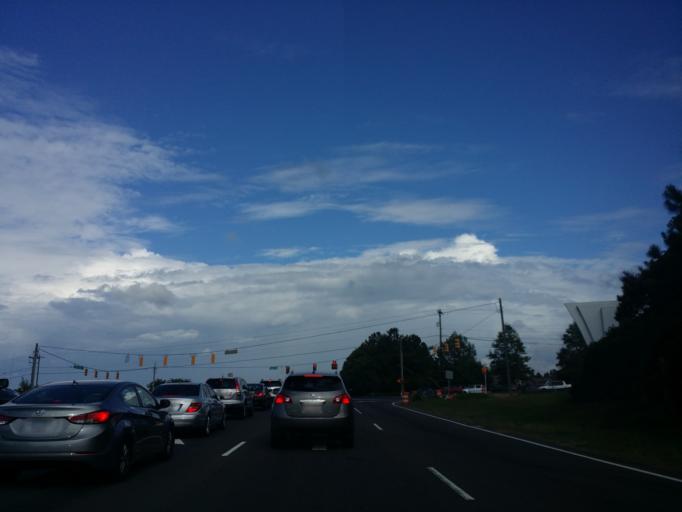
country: US
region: North Carolina
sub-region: Wake County
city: Morrisville
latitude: 35.9190
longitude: -78.8150
